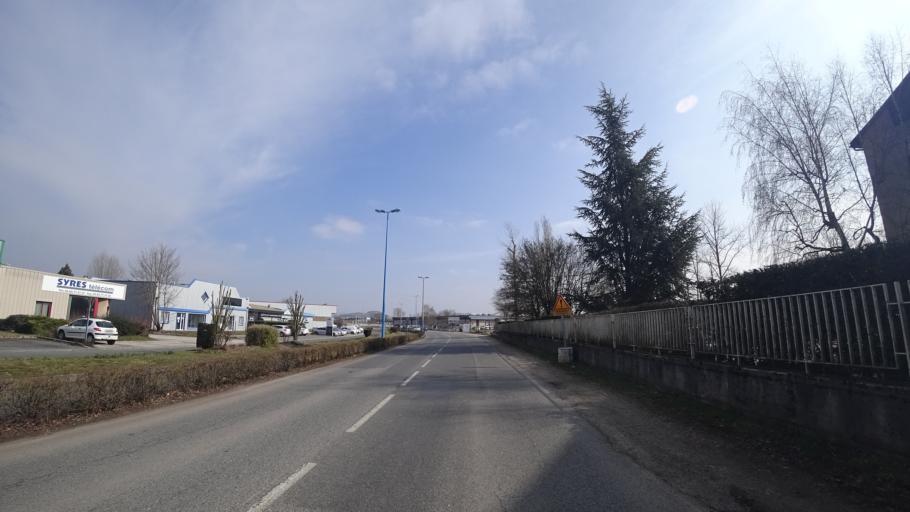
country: FR
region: Midi-Pyrenees
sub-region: Departement de l'Aveyron
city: Rodez
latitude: 44.3727
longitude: 2.5782
